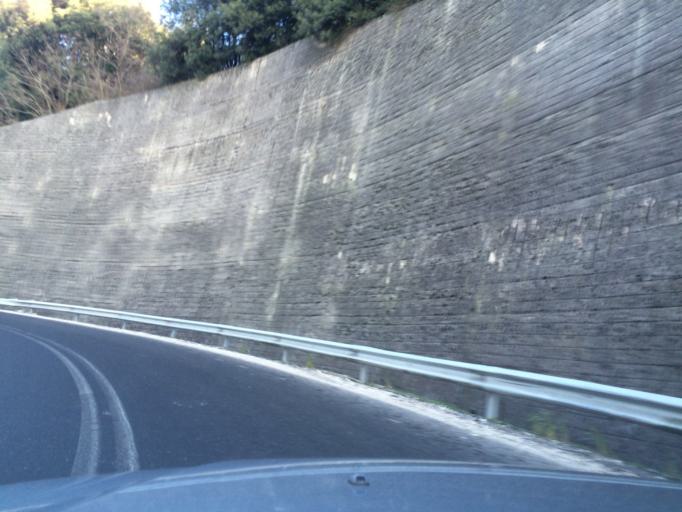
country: IT
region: Umbria
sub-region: Provincia di Terni
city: Fornole
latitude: 42.5296
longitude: 12.4739
